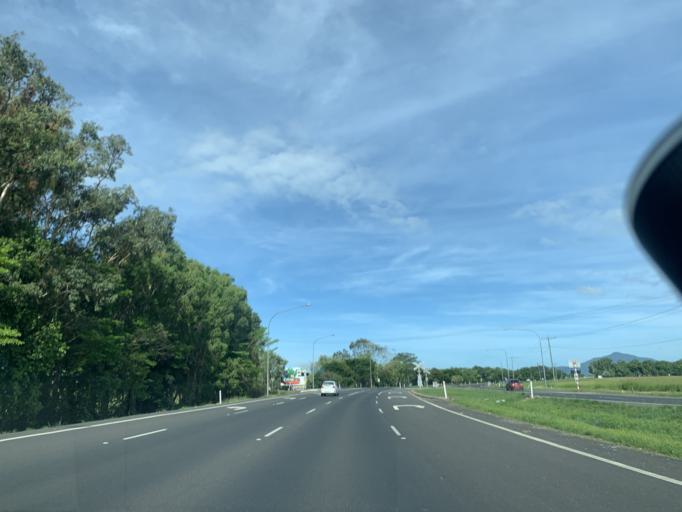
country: AU
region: Queensland
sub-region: Cairns
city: Redlynch
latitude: -16.8497
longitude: 145.7117
